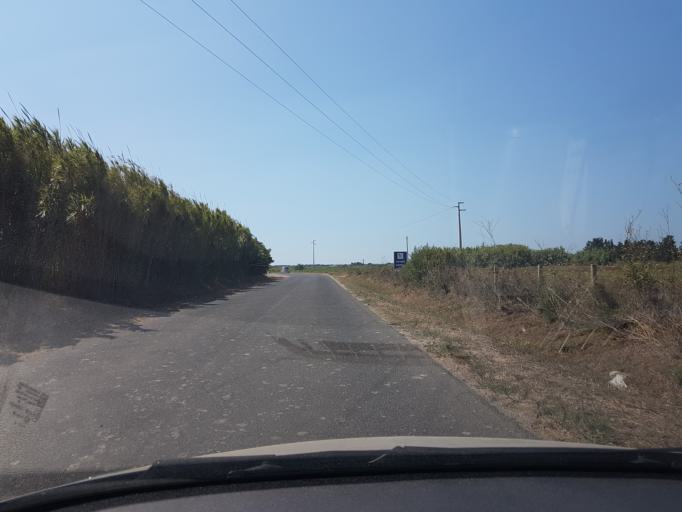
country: IT
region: Sardinia
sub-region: Provincia di Oristano
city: Riola Sardo
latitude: 40.0006
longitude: 8.5188
